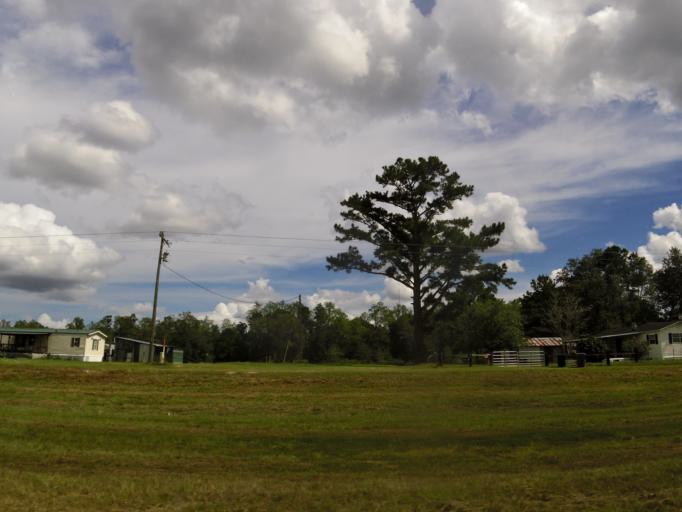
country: US
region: Georgia
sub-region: Brantley County
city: Nahunta
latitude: 31.1594
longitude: -81.9913
